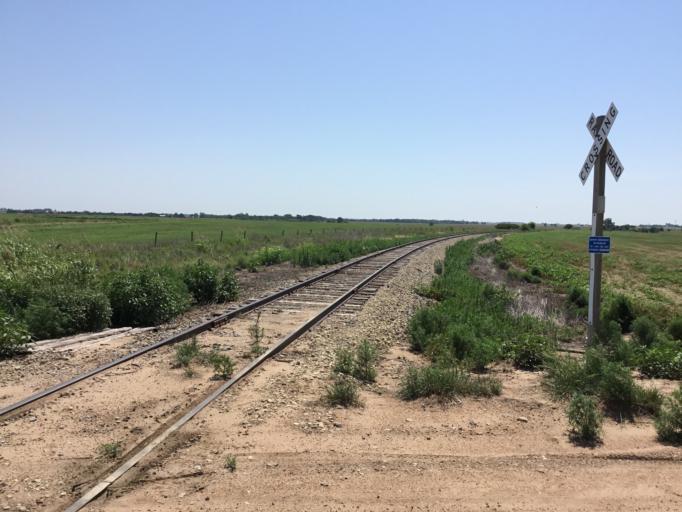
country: US
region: Kansas
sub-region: Kingman County
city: Kingman
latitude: 37.5529
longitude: -98.0992
